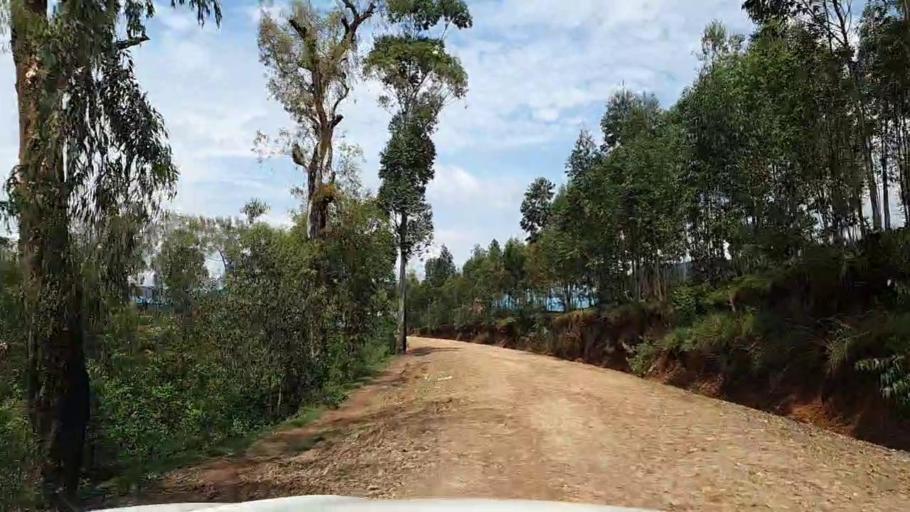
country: RW
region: Southern Province
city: Gikongoro
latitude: -2.3379
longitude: 29.5201
